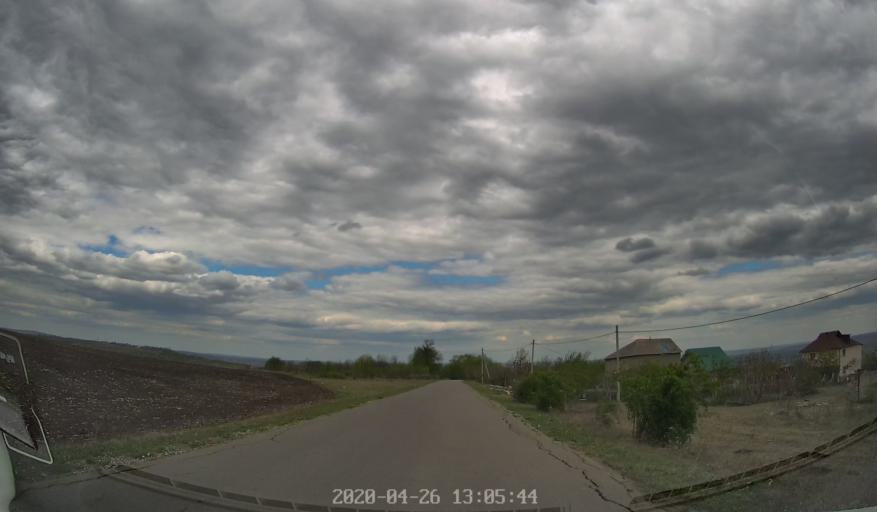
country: MD
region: Chisinau
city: Vadul lui Voda
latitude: 47.0784
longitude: 29.0669
